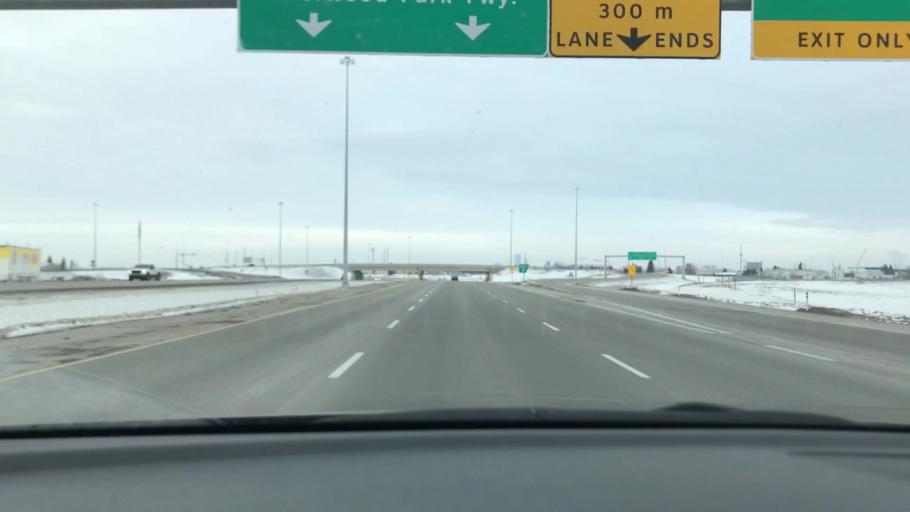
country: CA
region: Alberta
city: Sherwood Park
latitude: 53.5162
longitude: -113.3625
